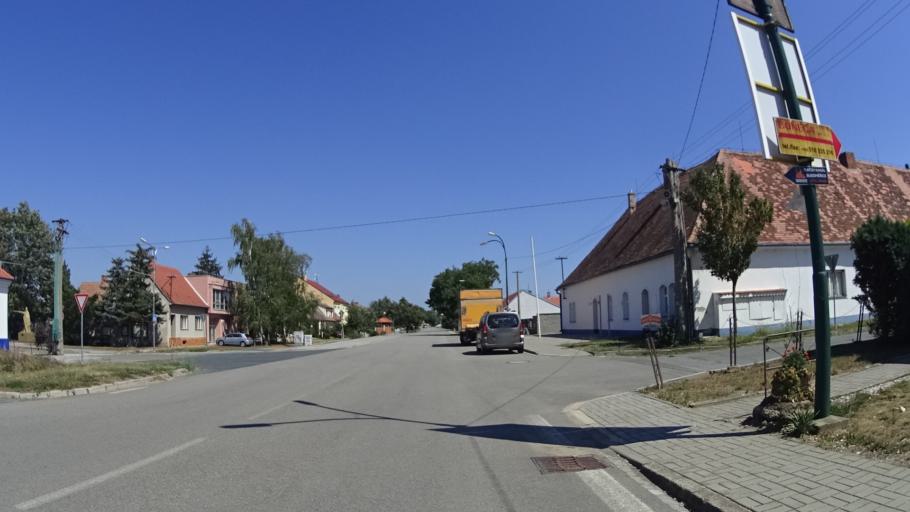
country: CZ
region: South Moravian
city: Sudomerice
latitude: 48.8669
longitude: 17.2567
